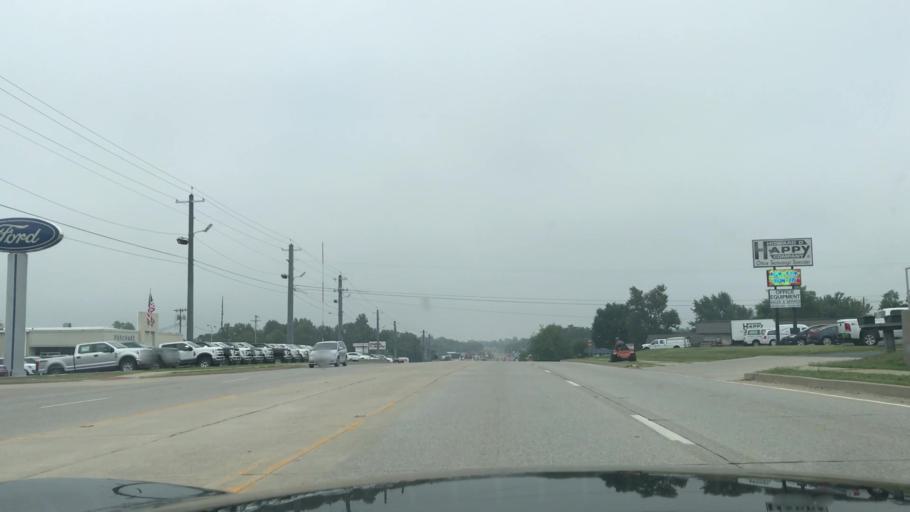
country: US
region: Kentucky
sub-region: Graves County
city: Mayfield
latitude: 36.7614
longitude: -88.6425
